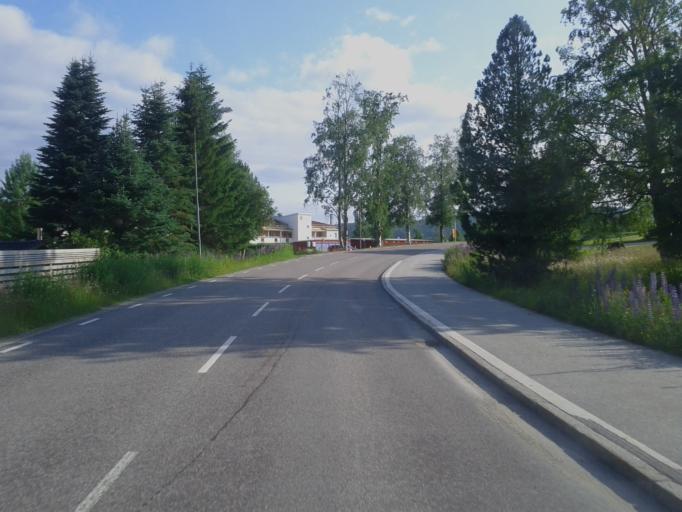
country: SE
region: Vaesternorrland
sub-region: OErnskoeldsviks Kommun
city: Ornskoldsvik
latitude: 63.2599
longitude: 18.7817
